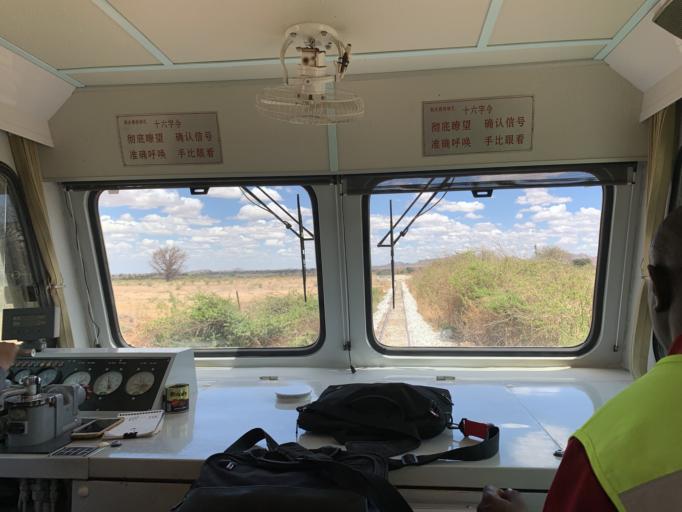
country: TZ
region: Dodoma
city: Dodoma
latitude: -6.1210
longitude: 35.5109
